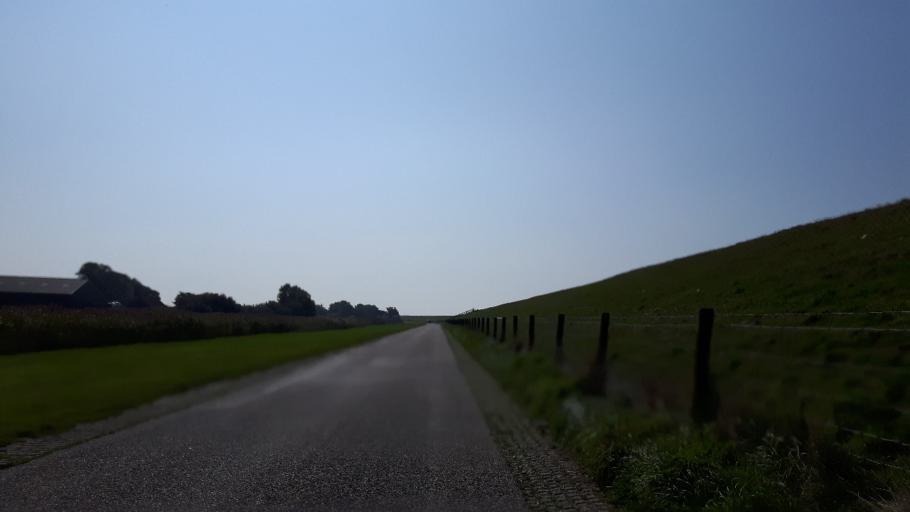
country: NL
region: Friesland
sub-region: Sudwest Fryslan
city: Makkum
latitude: 53.0877
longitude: 5.3819
